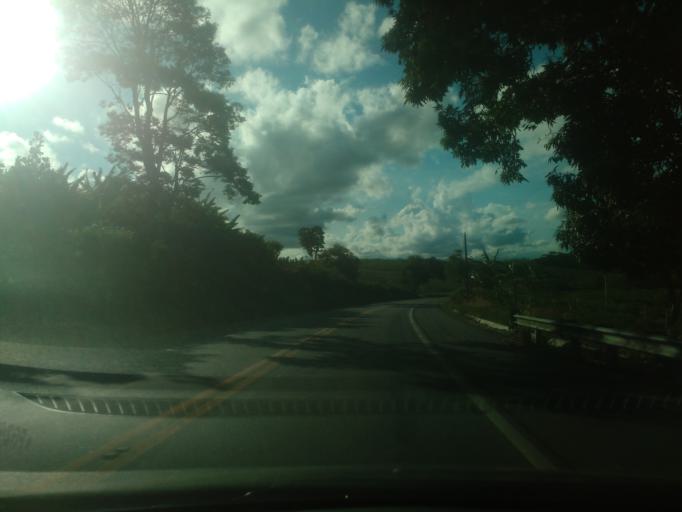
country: BR
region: Alagoas
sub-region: Messias
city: Messias
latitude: -9.3680
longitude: -35.8477
